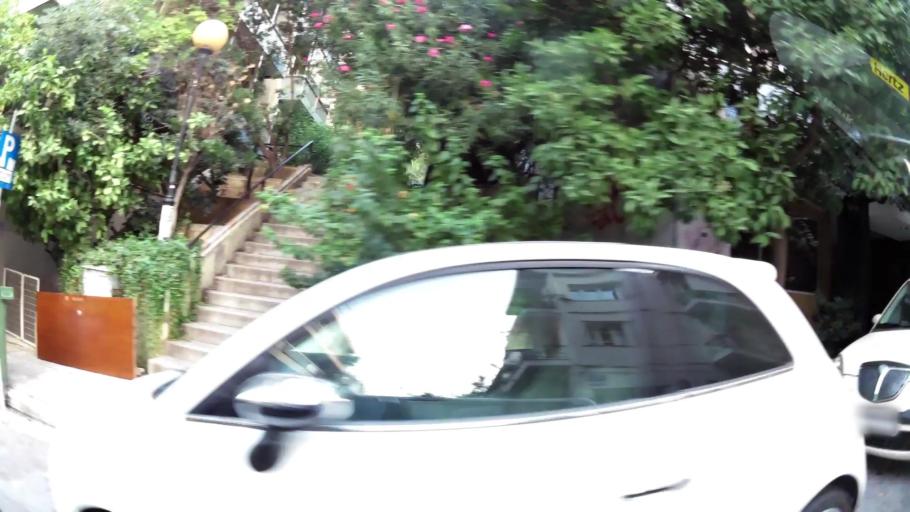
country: GR
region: Attica
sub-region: Nomarchia Athinas
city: Vyronas
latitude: 37.9792
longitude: 23.7430
